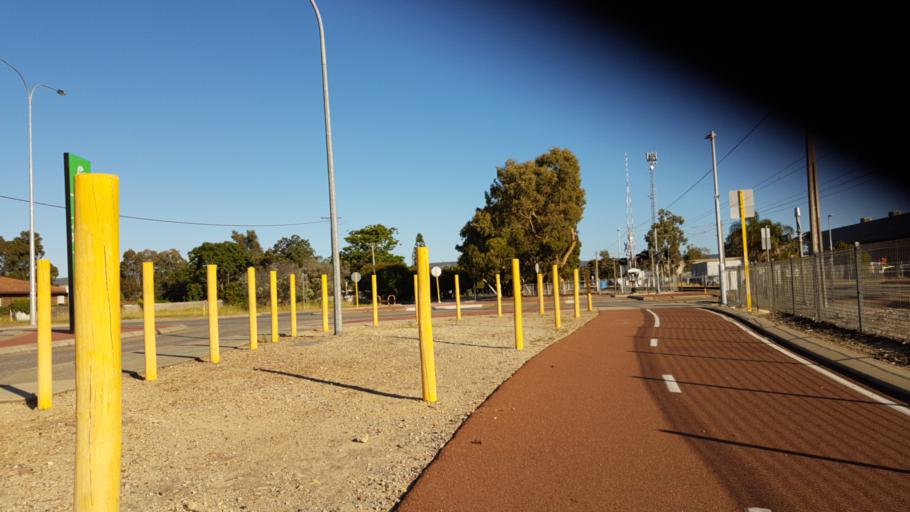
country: AU
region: Western Australia
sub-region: Gosnells
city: Maddington
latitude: -32.0498
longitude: 115.9841
